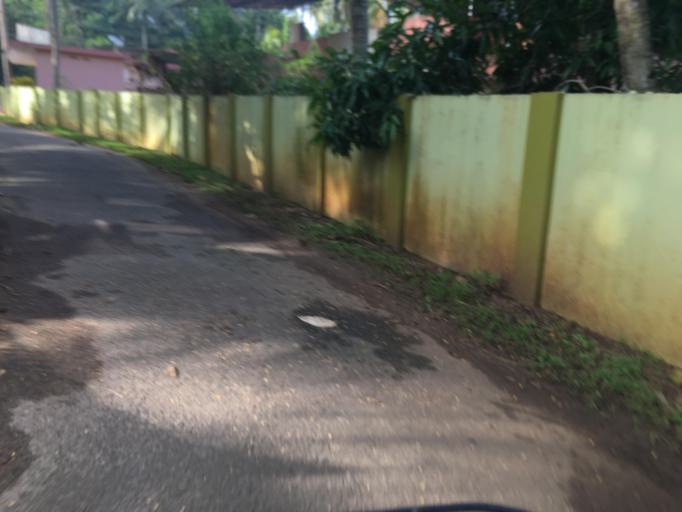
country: IN
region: Kerala
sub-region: Alappuzha
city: Kattanam
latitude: 9.2000
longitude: 76.5354
